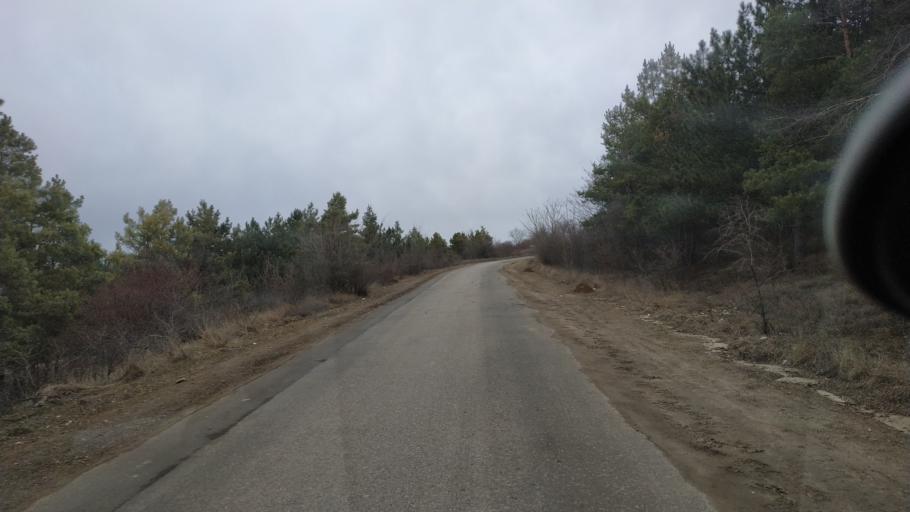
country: MD
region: Telenesti
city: Cocieri
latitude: 47.2684
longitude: 29.0769
